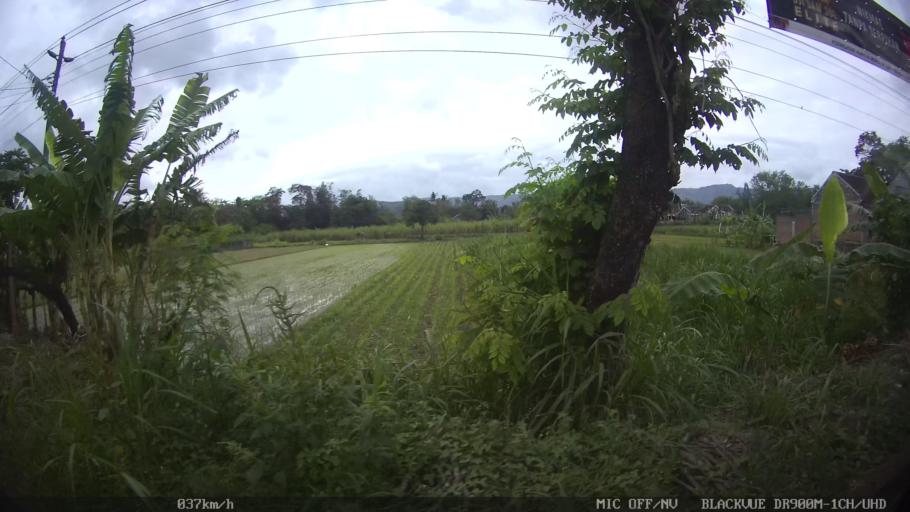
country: ID
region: Daerah Istimewa Yogyakarta
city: Sewon
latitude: -7.8720
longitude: 110.4074
